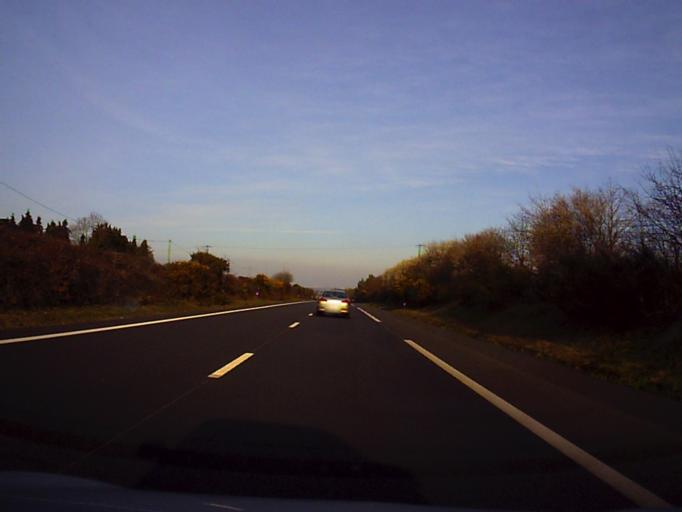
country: FR
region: Brittany
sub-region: Departement d'Ille-et-Vilaine
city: Monterfil
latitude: 48.0353
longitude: -1.9774
